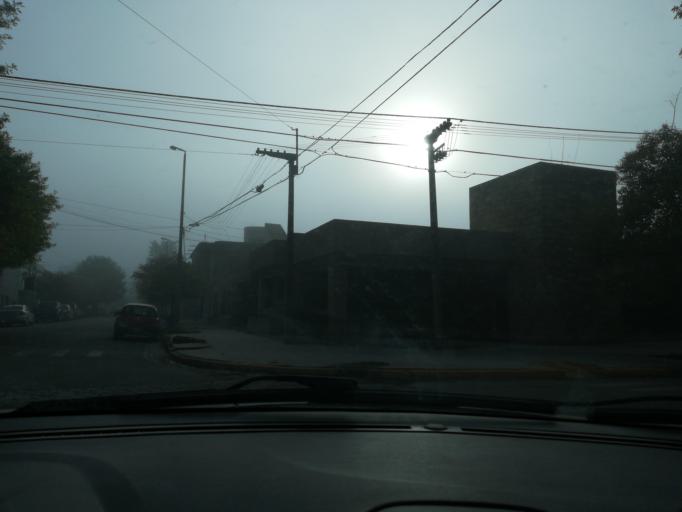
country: AR
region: Buenos Aires
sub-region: Partido de Balcarce
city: Balcarce
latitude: -37.8512
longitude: -58.2592
